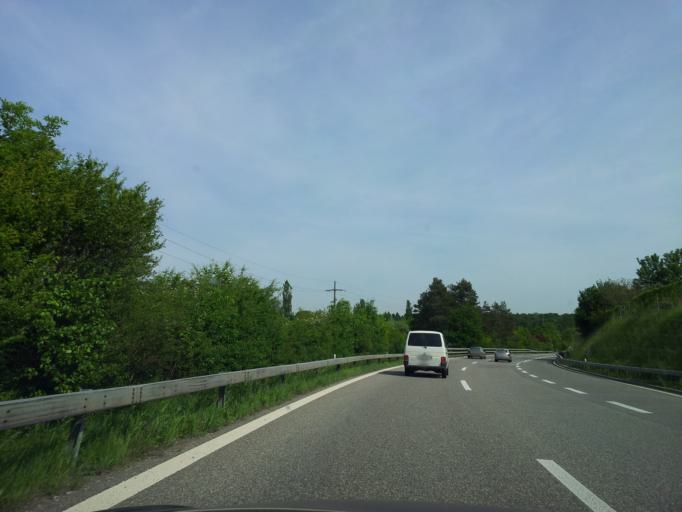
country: CH
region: Zurich
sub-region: Bezirk Buelach
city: Buelach / Niederflachs
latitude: 47.5146
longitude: 8.5256
